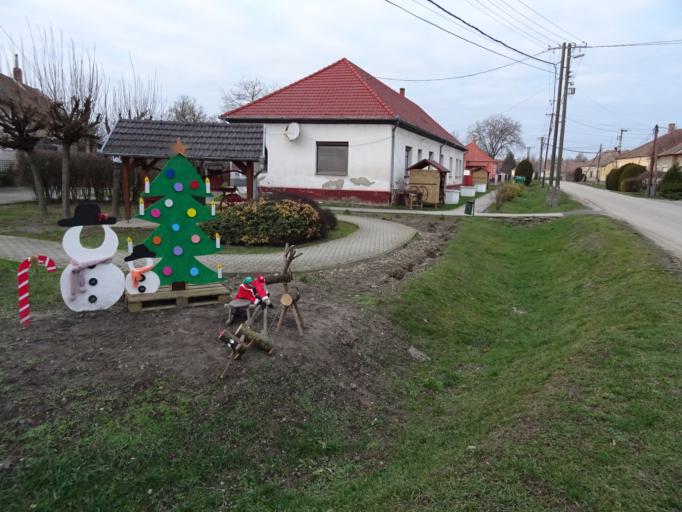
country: HU
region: Gyor-Moson-Sopron
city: Farad
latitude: 47.5366
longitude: 17.2081
